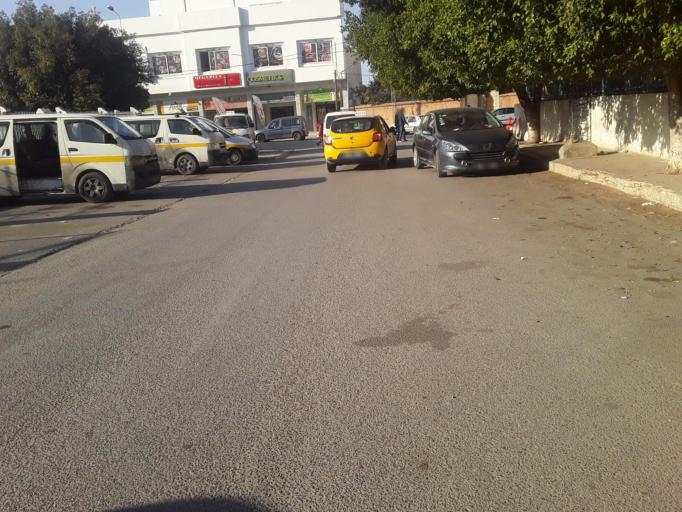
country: TN
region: Al Qayrawan
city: Kairouan
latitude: 35.6812
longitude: 10.0998
